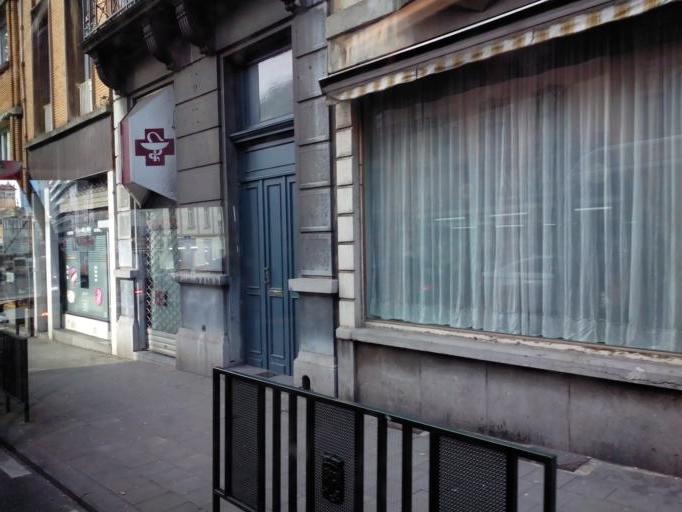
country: BE
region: Brussels Capital
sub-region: Bruxelles-Capitale
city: Brussels
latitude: 50.8487
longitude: 4.3784
